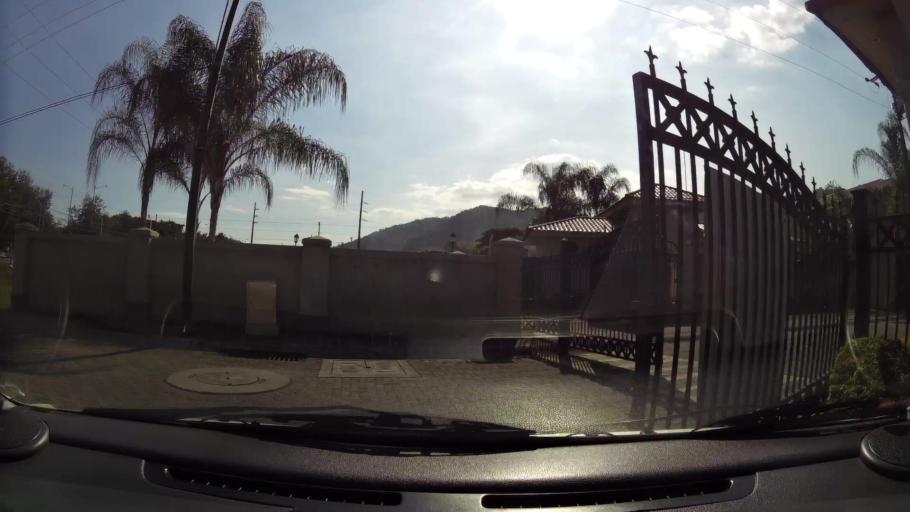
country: EC
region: Guayas
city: Santa Lucia
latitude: -2.1825
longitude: -79.9866
